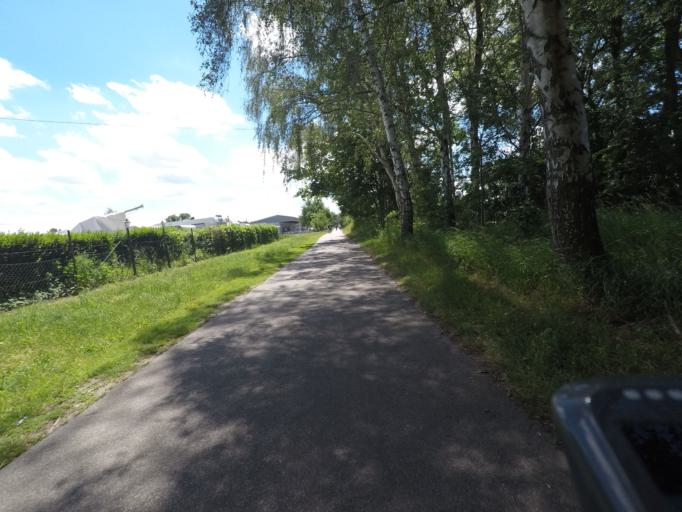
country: DE
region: Lower Saxony
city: Winsen
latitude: 53.4097
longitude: 10.1799
